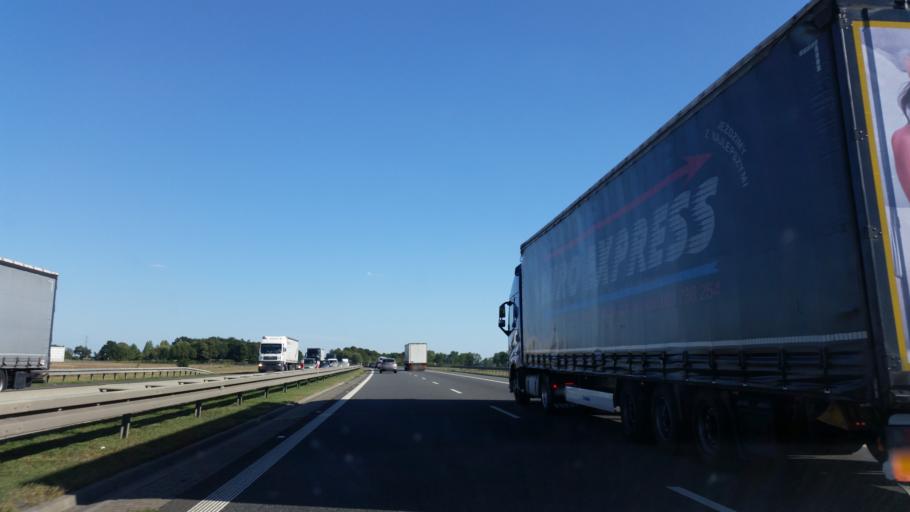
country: PL
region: Lower Silesian Voivodeship
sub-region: Powiat wroclawski
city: Zorawina
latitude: 51.0075
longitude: 17.0311
